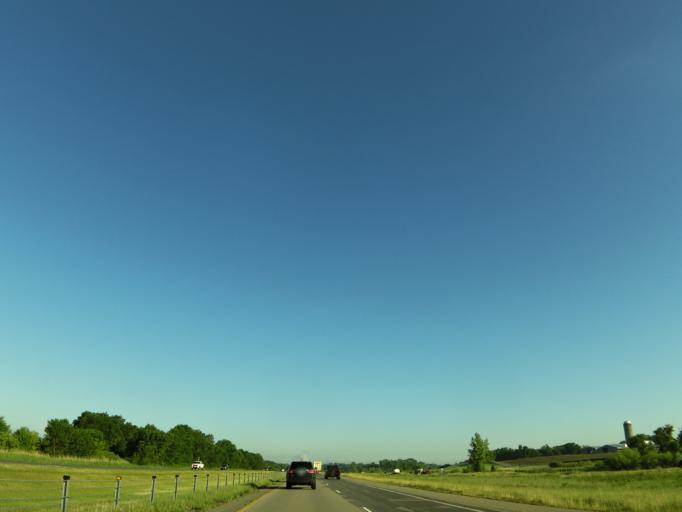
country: US
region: Minnesota
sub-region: Sherburne County
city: Big Lake
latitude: 45.2682
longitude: -93.7227
